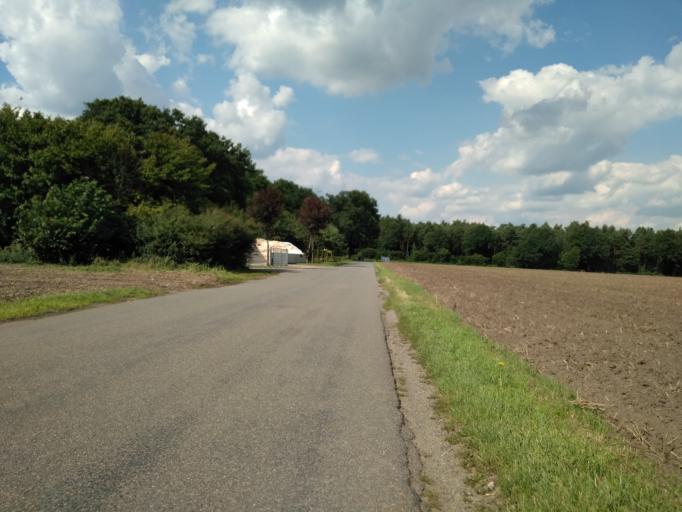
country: DE
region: North Rhine-Westphalia
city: Dorsten
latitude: 51.7311
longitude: 6.9729
